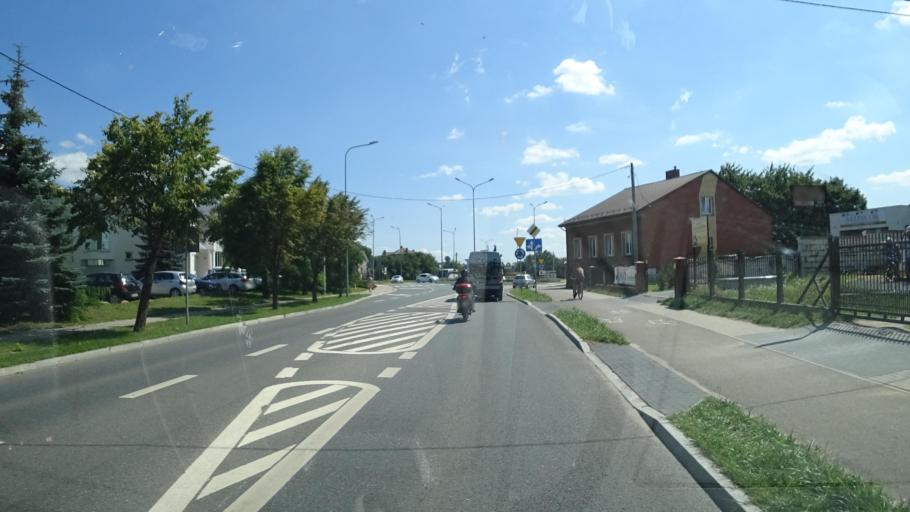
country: PL
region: Podlasie
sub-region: Lomza
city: Lomza
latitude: 53.1727
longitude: 22.0810
